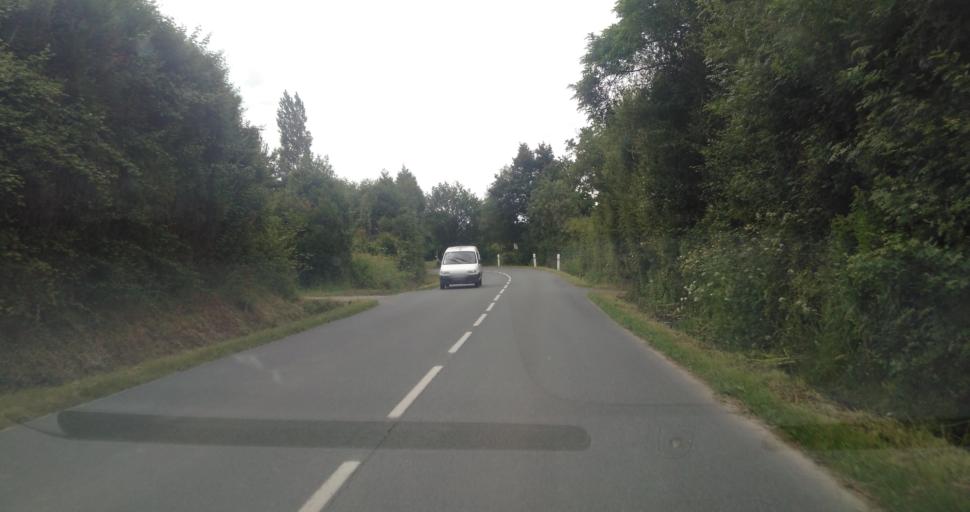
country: FR
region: Pays de la Loire
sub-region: Departement de la Vendee
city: La Chaize-le-Vicomte
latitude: 46.6845
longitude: -1.3023
